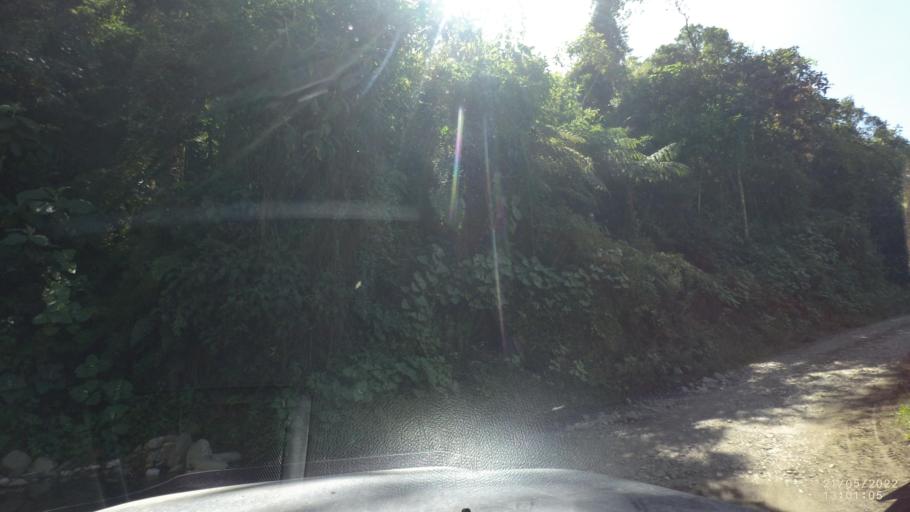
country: BO
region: Cochabamba
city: Colomi
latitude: -17.1629
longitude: -65.9522
